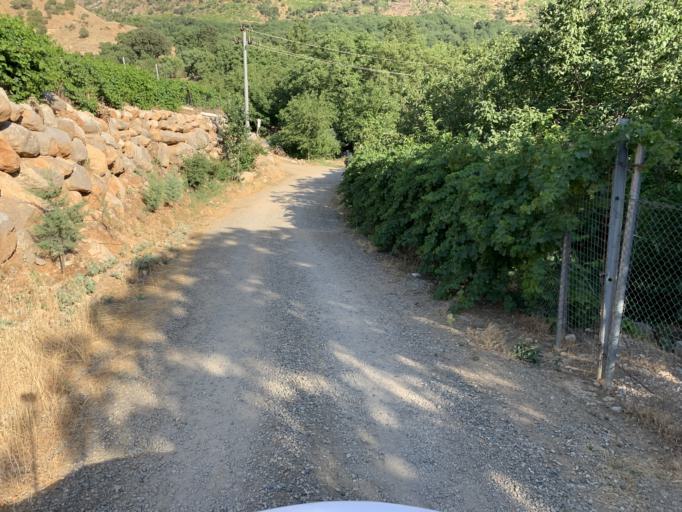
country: IQ
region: As Sulaymaniyah
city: Qeladize
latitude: 35.9893
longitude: 45.2001
